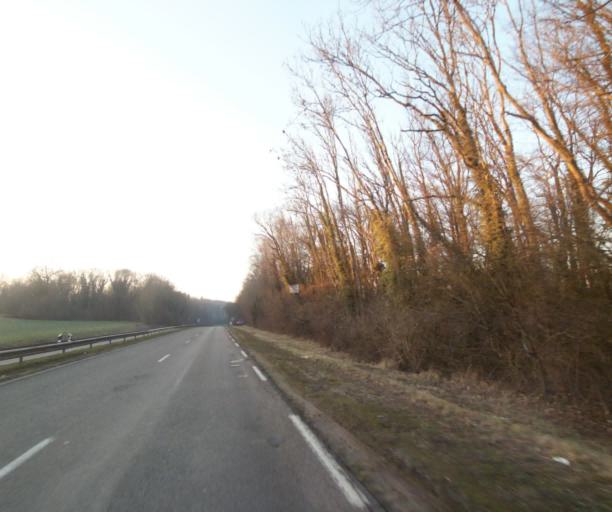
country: FR
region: Lorraine
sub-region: Departement de la Meuse
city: Ancerville
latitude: 48.6101
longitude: 5.0096
